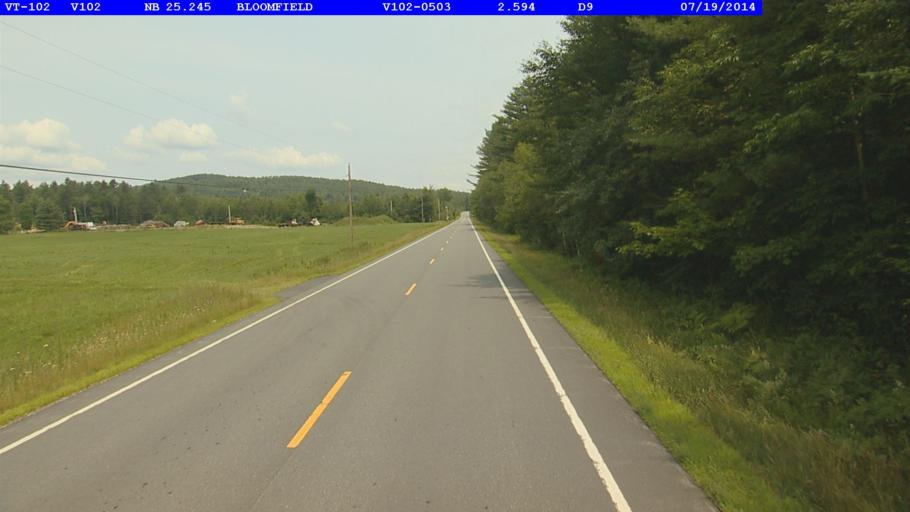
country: US
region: New Hampshire
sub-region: Coos County
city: Stratford
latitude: 44.7758
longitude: -71.6003
